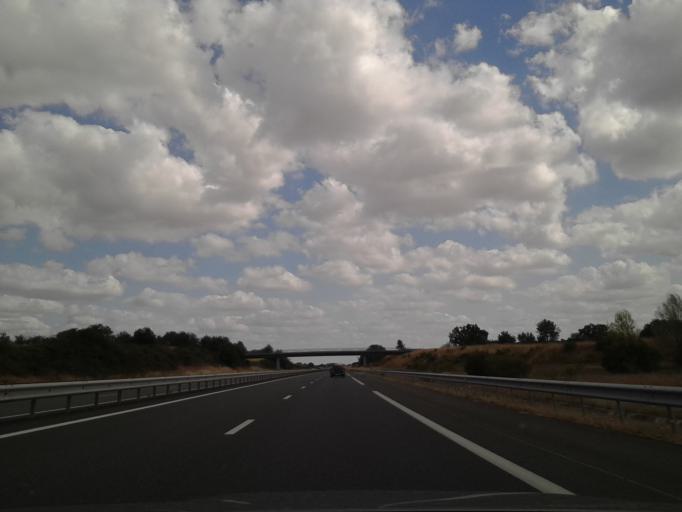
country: FR
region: Centre
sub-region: Departement du Cher
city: Saint-Amand-Montrond
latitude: 46.6304
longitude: 2.5009
